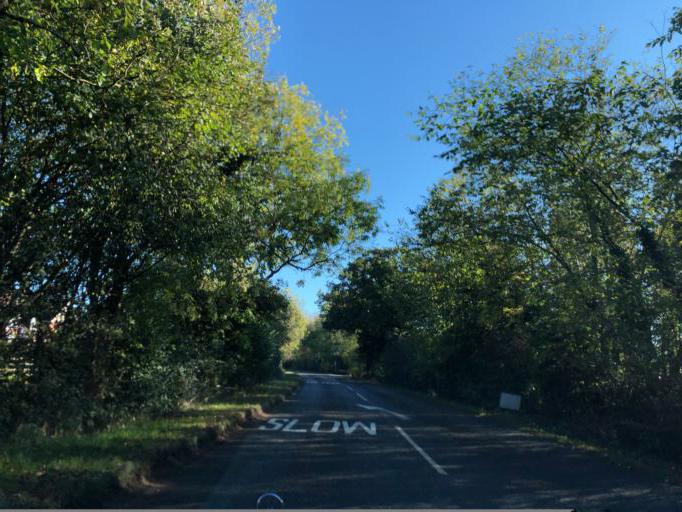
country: GB
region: England
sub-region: Warwickshire
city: Royal Leamington Spa
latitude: 52.2641
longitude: -1.5471
